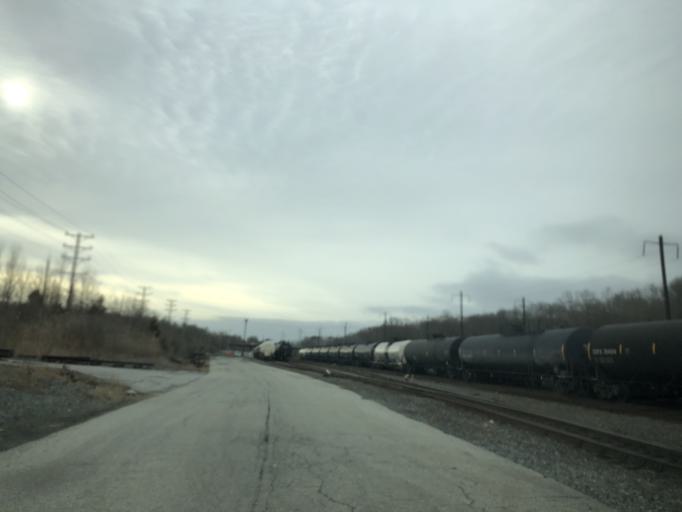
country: US
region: Delaware
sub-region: New Castle County
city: Newark
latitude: 39.6651
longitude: -75.7665
